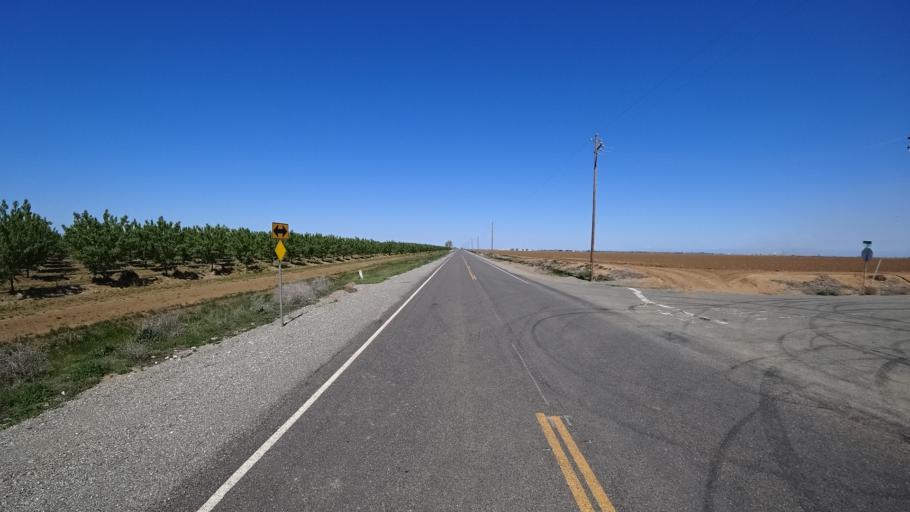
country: US
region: California
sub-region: Glenn County
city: Willows
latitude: 39.4521
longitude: -122.2488
